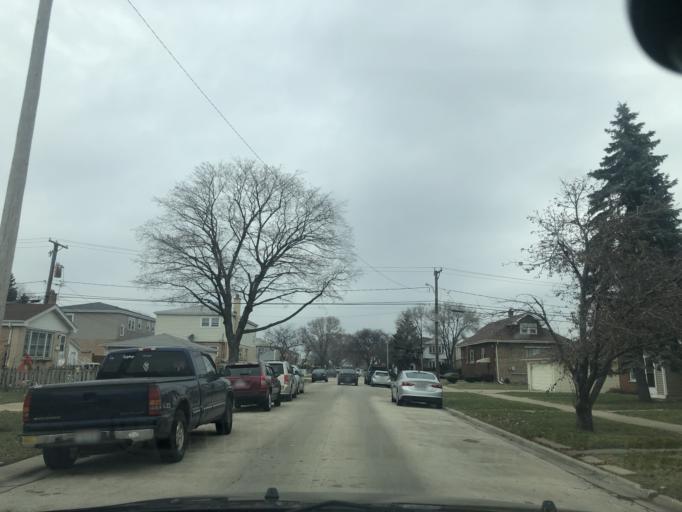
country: US
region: Illinois
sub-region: Cook County
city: Schiller Park
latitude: 41.9686
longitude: -87.8686
